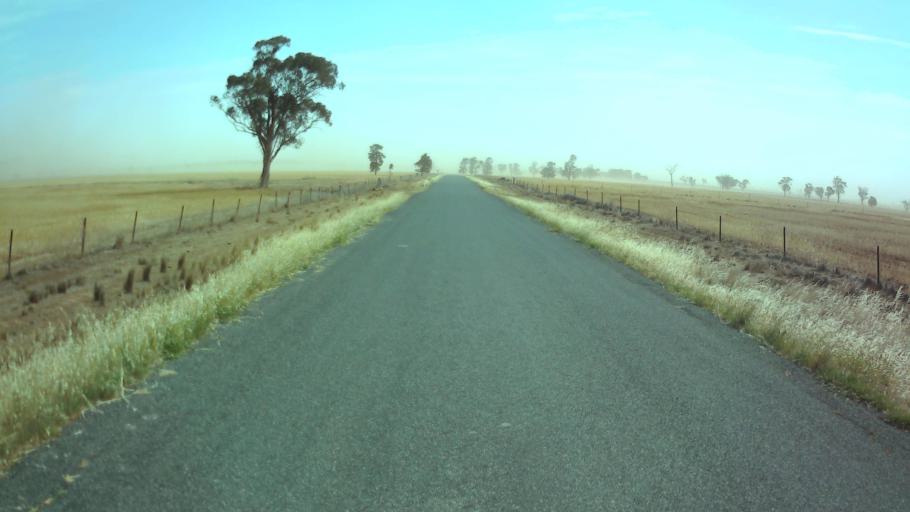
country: AU
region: New South Wales
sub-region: Weddin
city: Grenfell
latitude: -33.7416
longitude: 147.9925
